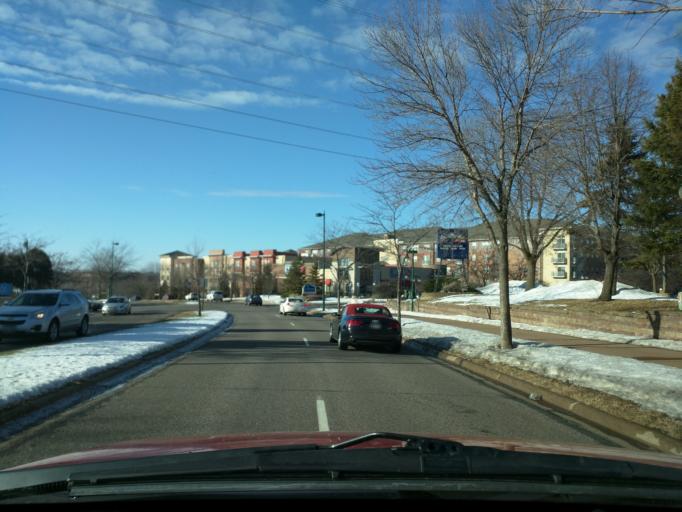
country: US
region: Minnesota
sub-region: Hennepin County
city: Eden Prairie
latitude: 44.8572
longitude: -93.4313
